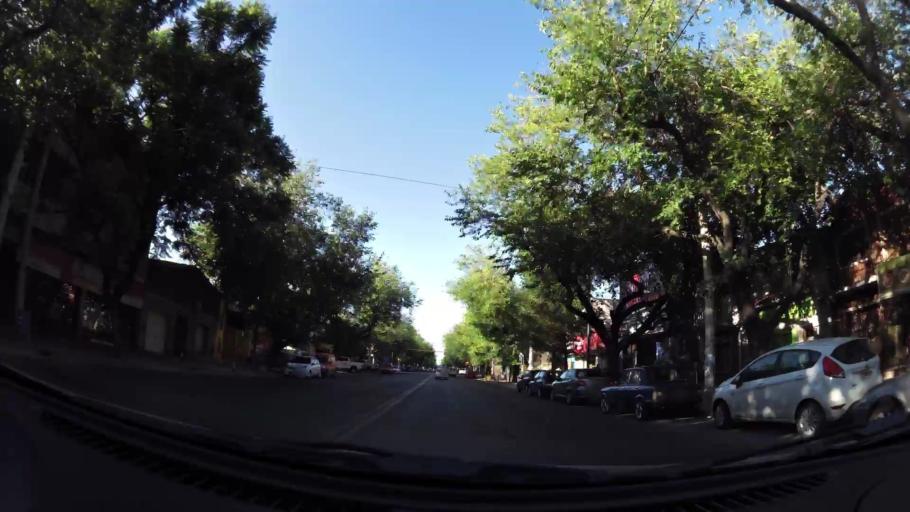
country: AR
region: Mendoza
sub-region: Departamento de Godoy Cruz
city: Godoy Cruz
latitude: -32.9202
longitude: -68.8472
